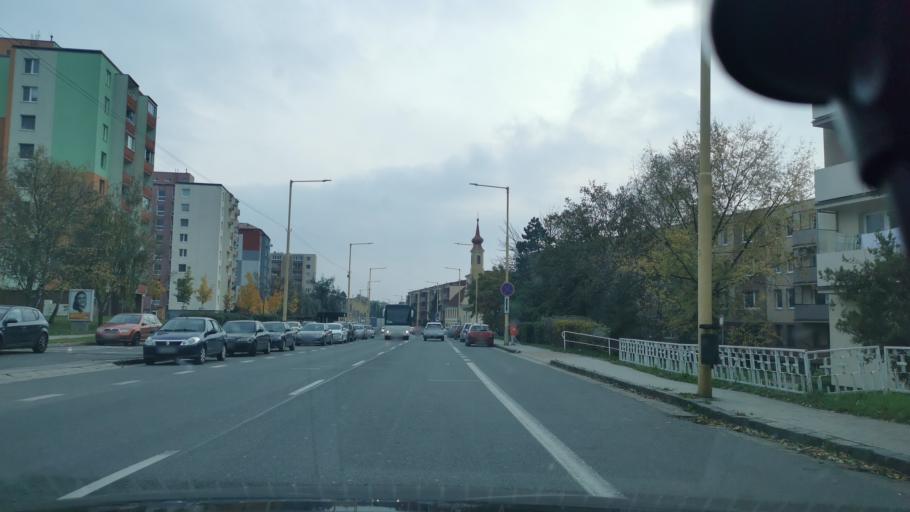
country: SK
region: Trnavsky
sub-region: Okres Skalica
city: Holic
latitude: 48.8071
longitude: 17.1624
